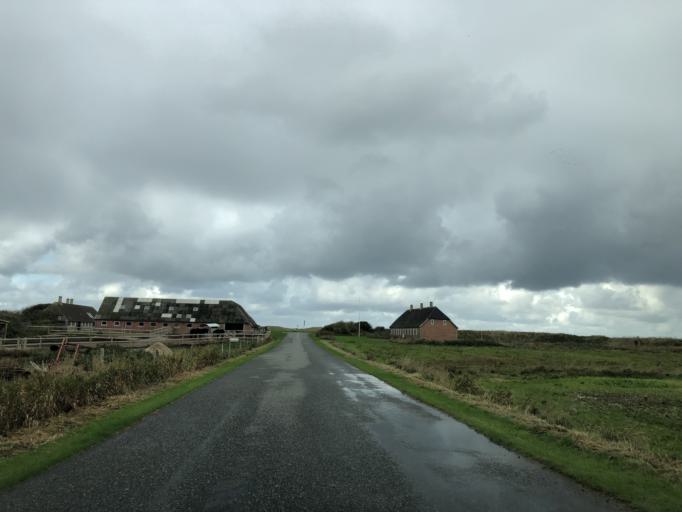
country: DK
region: Central Jutland
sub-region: Lemvig Kommune
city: Harboore
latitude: 56.4738
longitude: 8.1347
